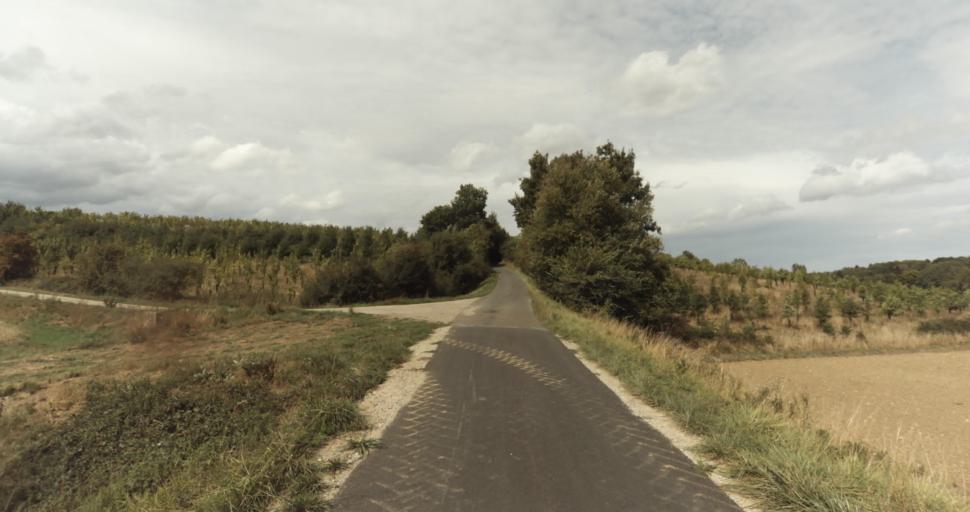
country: FR
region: Lower Normandy
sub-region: Departement du Calvados
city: Orbec
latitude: 48.9121
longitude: 0.3834
